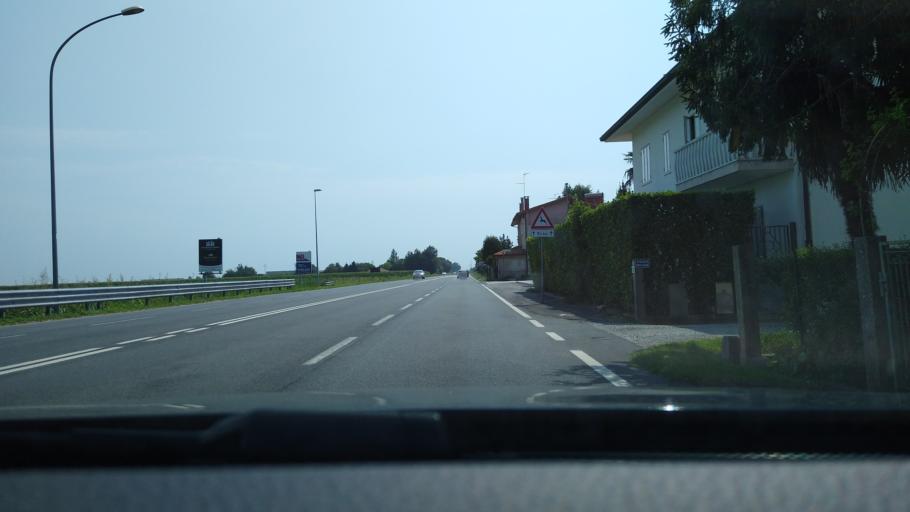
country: IT
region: Friuli Venezia Giulia
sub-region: Provincia di Udine
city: Pertegada
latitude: 45.7154
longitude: 13.0514
